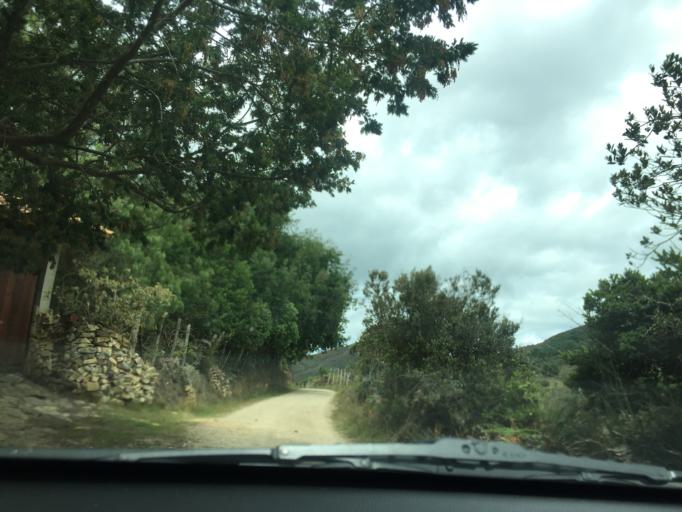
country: CO
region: Cundinamarca
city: Tocancipa
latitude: 4.9595
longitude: -73.8895
